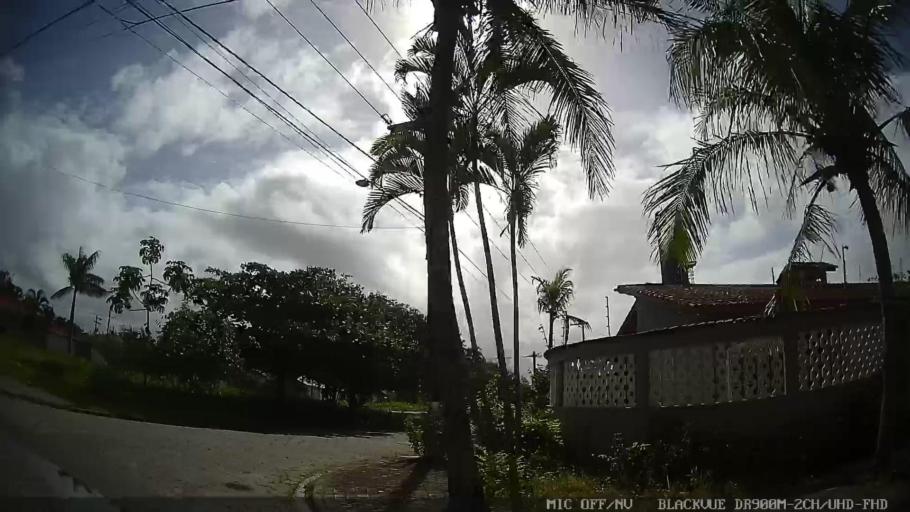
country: BR
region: Sao Paulo
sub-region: Mongagua
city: Mongagua
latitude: -24.1331
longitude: -46.6957
